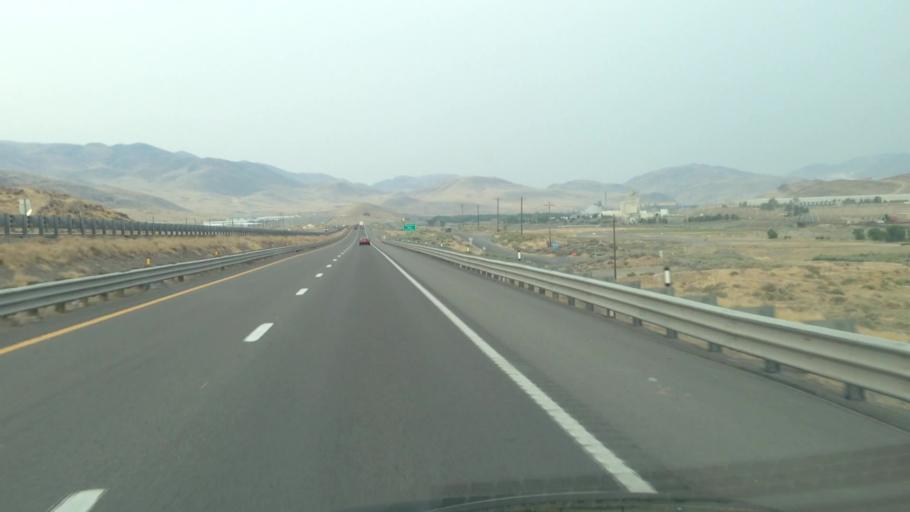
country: US
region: Nevada
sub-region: Washoe County
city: Spanish Springs
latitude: 39.5522
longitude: -119.5692
